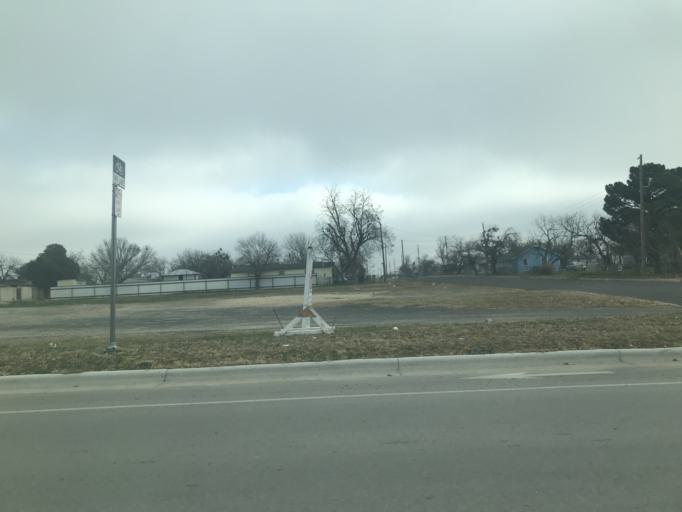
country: US
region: Texas
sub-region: Tom Green County
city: San Angelo
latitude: 31.4807
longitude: -100.4537
